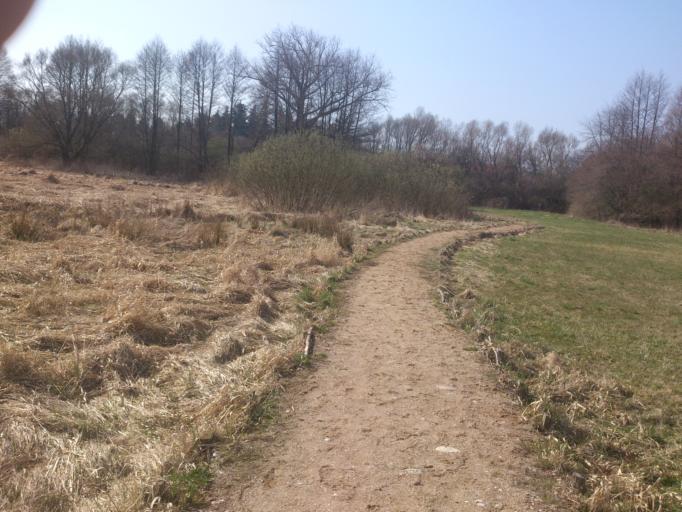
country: PL
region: Podlasie
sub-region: Powiat bialostocki
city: Tykocin
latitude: 53.1075
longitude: 22.7972
